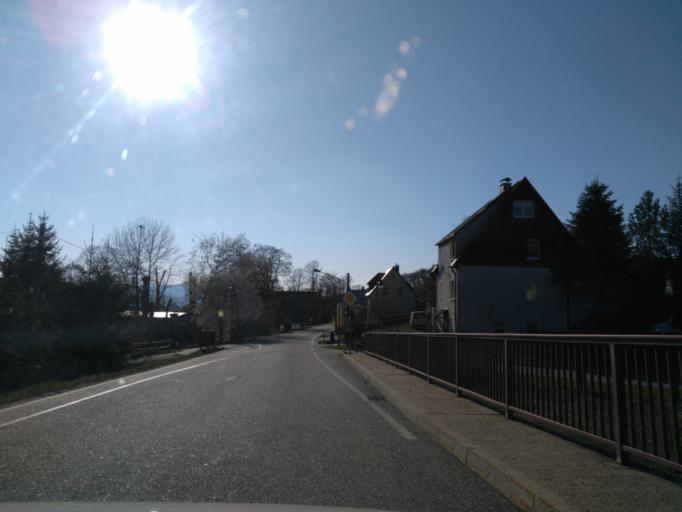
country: DE
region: Saxony
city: Scheibenberg
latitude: 50.5363
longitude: 12.9034
